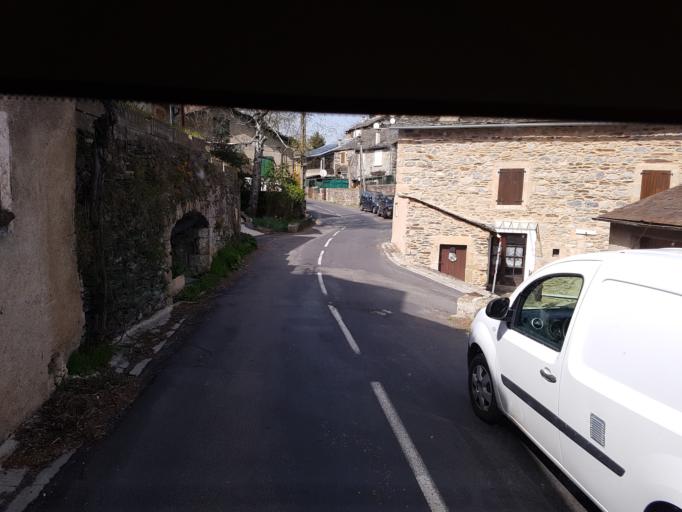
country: FR
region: Languedoc-Roussillon
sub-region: Departement de la Lozere
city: Florac
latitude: 44.2288
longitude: 3.5771
